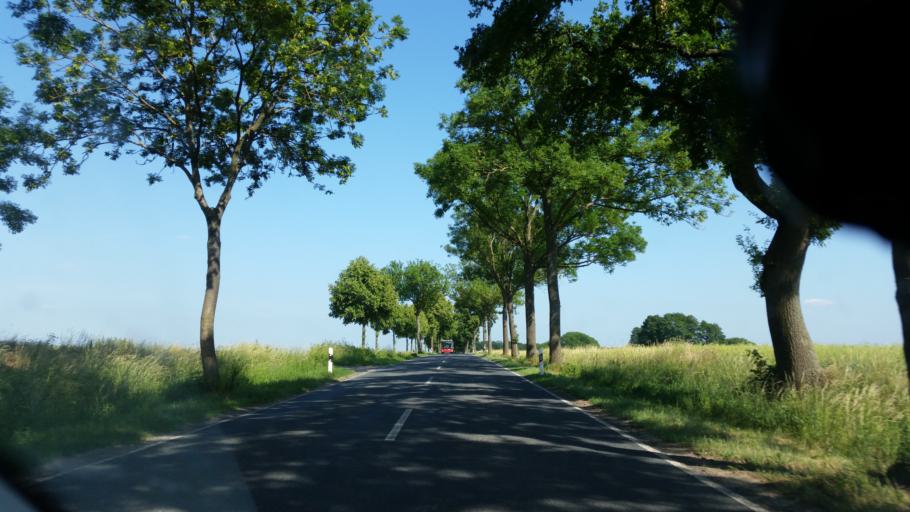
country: DE
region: Lower Saxony
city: Wolfsburg
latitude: 52.3455
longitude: 10.7926
